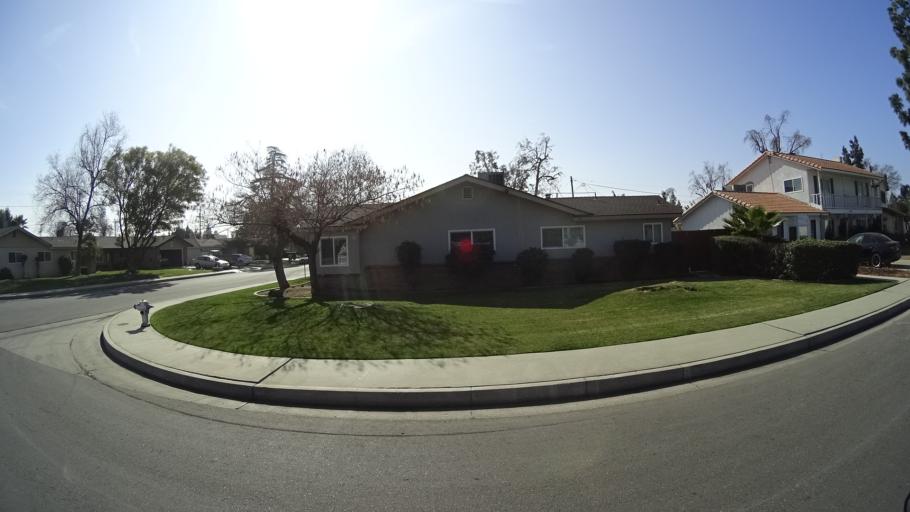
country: US
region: California
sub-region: Kern County
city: Bakersfield
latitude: 35.3351
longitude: -119.0550
